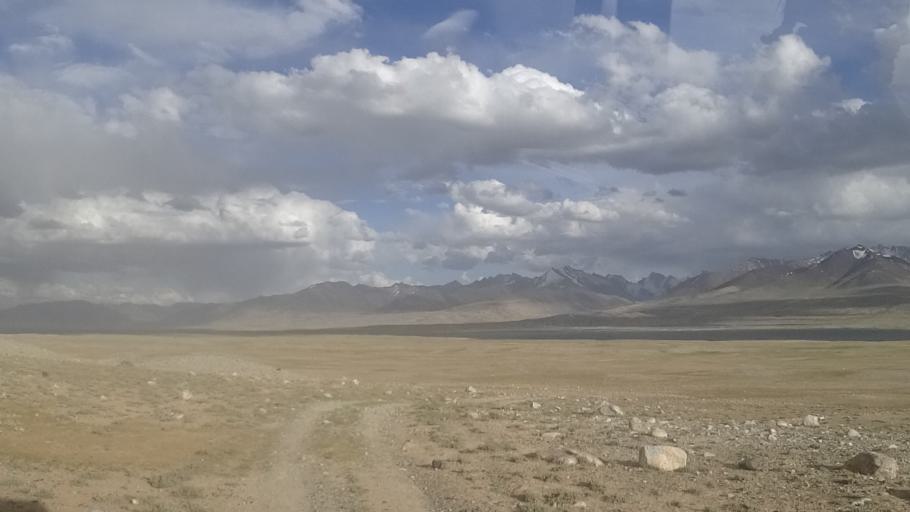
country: TJ
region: Gorno-Badakhshan
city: Murghob
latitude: 37.4641
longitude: 73.6132
